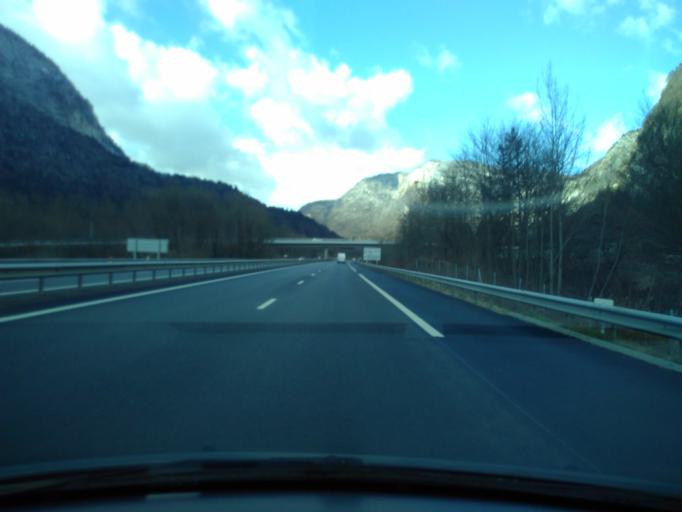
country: FR
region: Rhone-Alpes
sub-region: Departement de la Haute-Savoie
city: Magland
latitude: 46.0187
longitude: 6.6197
